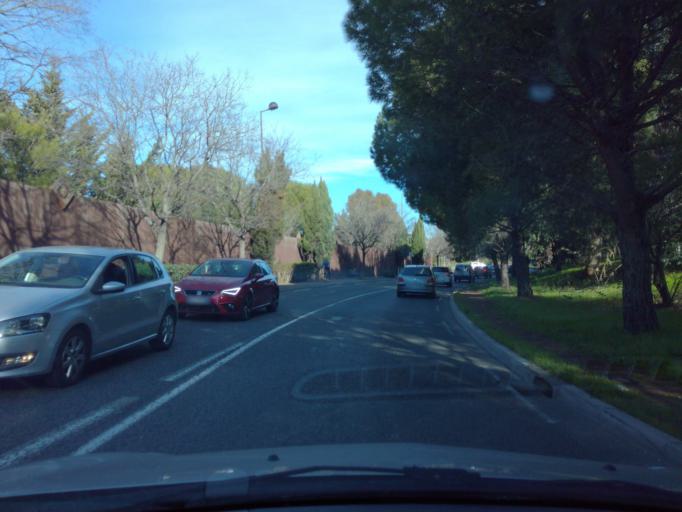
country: FR
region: Provence-Alpes-Cote d'Azur
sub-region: Departement des Alpes-Maritimes
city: Vallauris
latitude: 43.5770
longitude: 7.0902
